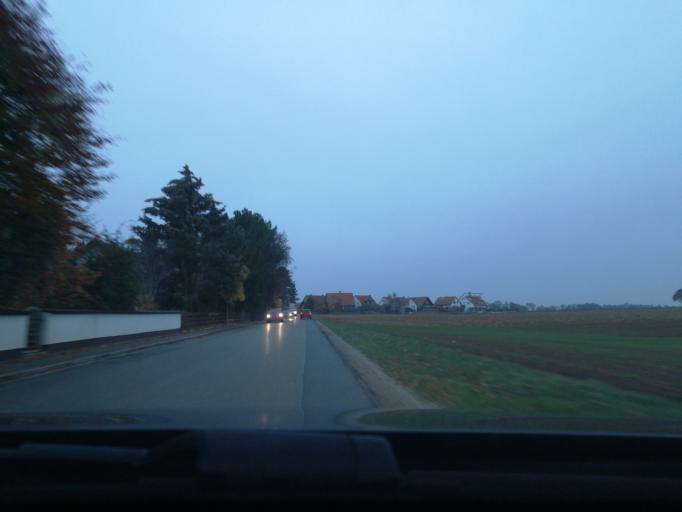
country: DE
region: Bavaria
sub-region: Regierungsbezirk Mittelfranken
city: Obermichelbach
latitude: 49.5125
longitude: 10.9289
